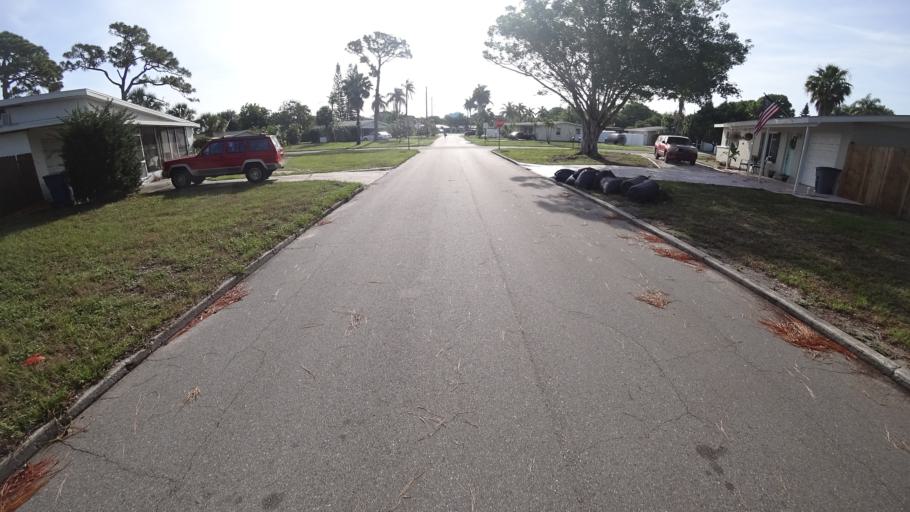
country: US
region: Florida
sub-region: Manatee County
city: West Bradenton
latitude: 27.4978
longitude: -82.6218
